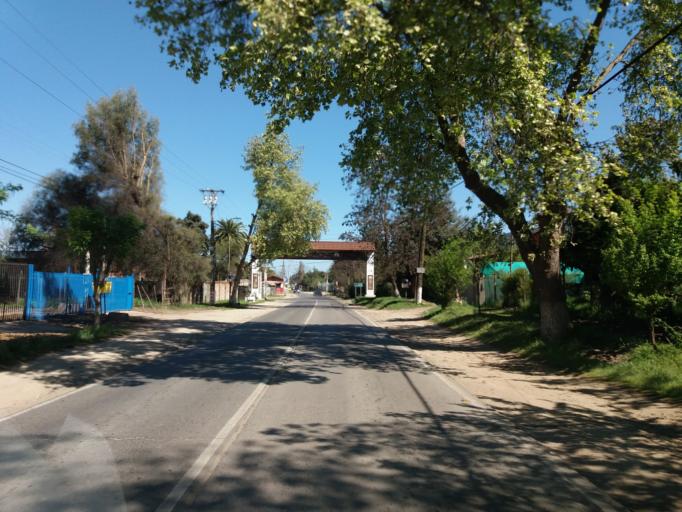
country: CL
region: Valparaiso
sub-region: Provincia de Marga Marga
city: Limache
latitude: -32.9976
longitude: -71.2194
